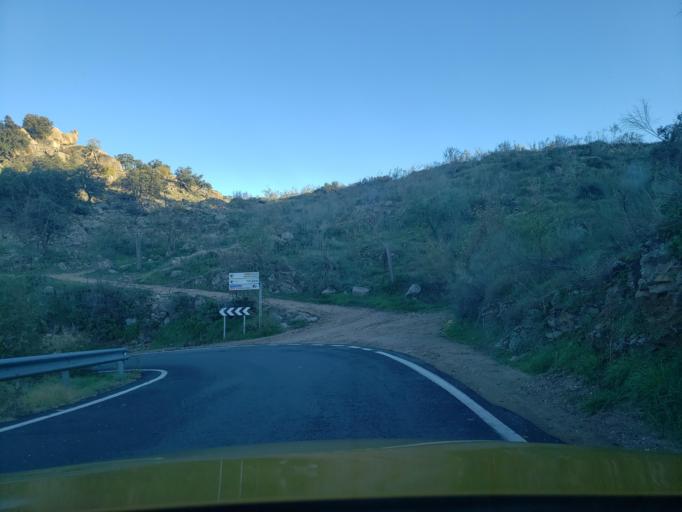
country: ES
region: Castille-La Mancha
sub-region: Province of Toledo
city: Toledo
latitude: 39.8500
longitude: -4.0214
